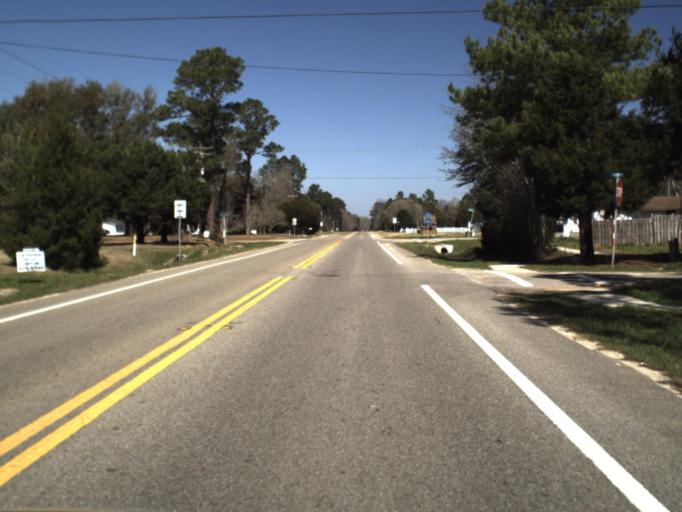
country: US
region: Florida
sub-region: Calhoun County
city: Blountstown
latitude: 30.4744
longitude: -85.0451
